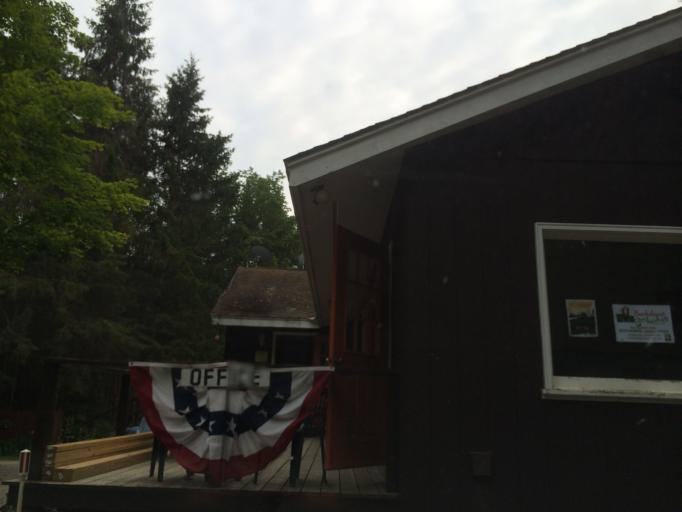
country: US
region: Massachusetts
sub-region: Berkshire County
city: Lanesborough
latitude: 42.5505
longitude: -73.2300
